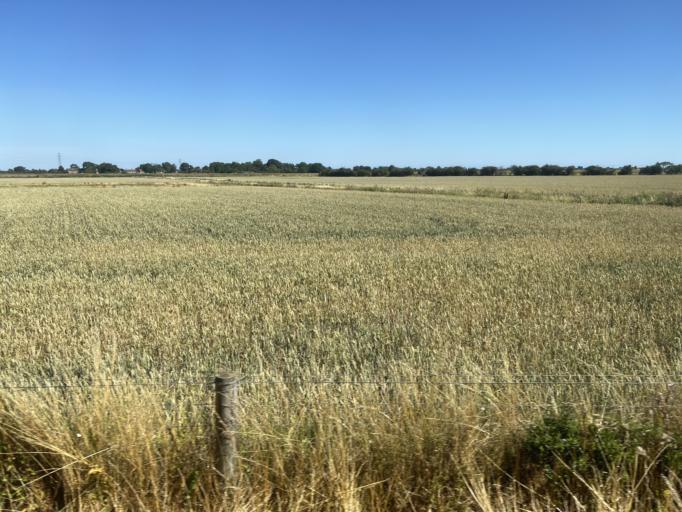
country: GB
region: England
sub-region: Lincolnshire
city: Wainfleet All Saints
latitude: 53.1163
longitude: 0.2106
